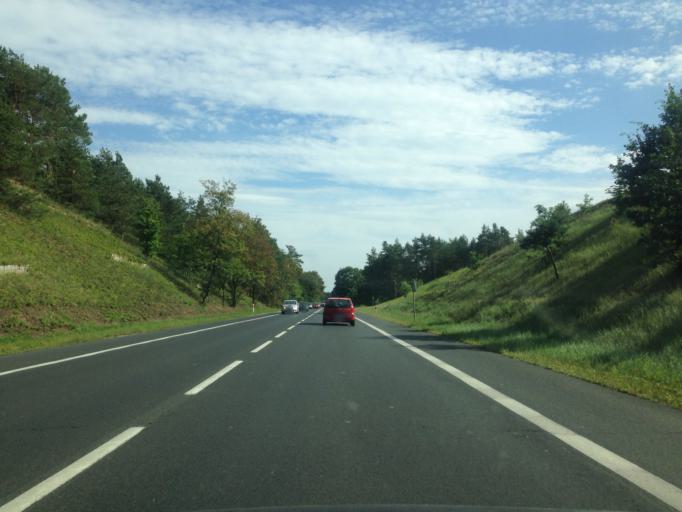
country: PL
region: Kujawsko-Pomorskie
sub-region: Powiat aleksandrowski
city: Aleksandrow Kujawski
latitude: 52.8997
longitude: 18.7260
